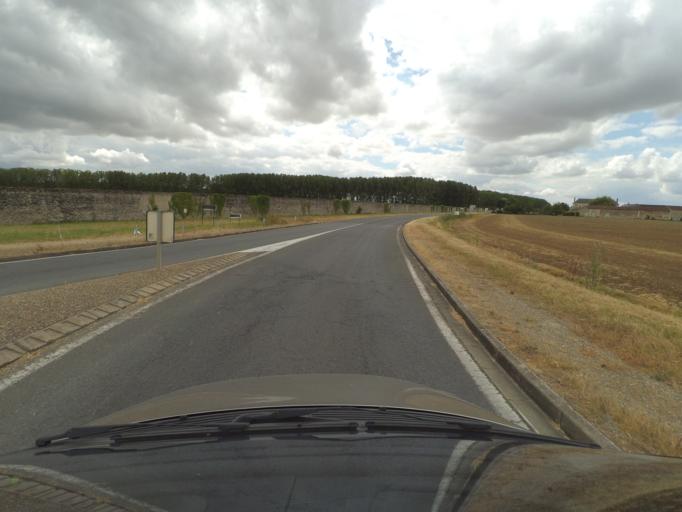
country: FR
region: Centre
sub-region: Departement d'Indre-et-Loire
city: Richelieu
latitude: 47.0012
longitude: 0.3189
